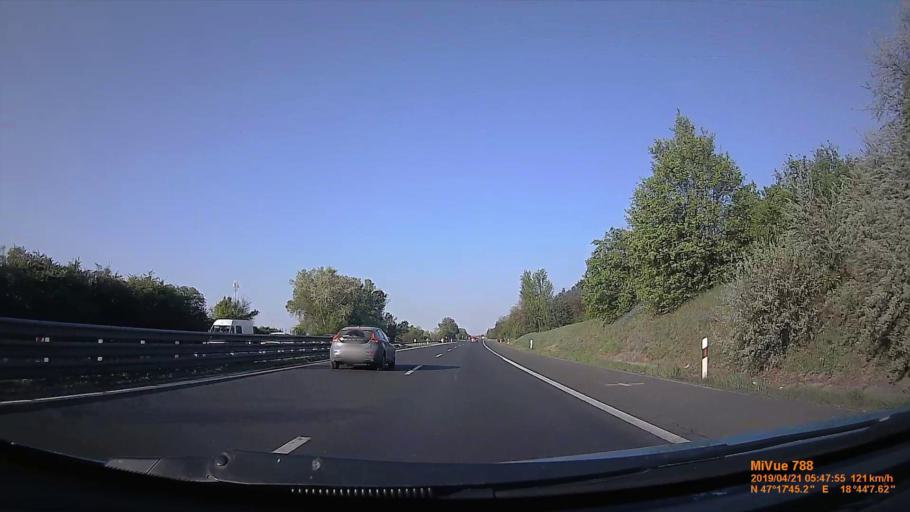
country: HU
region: Fejer
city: Baracska
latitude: 47.2944
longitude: 18.7347
